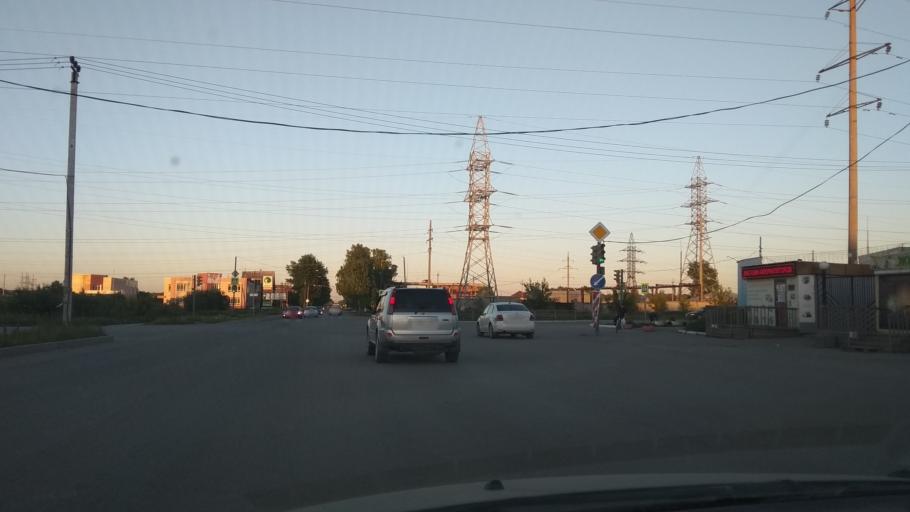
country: RU
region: Sverdlovsk
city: Sredneuralsk
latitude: 56.9917
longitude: 60.4782
